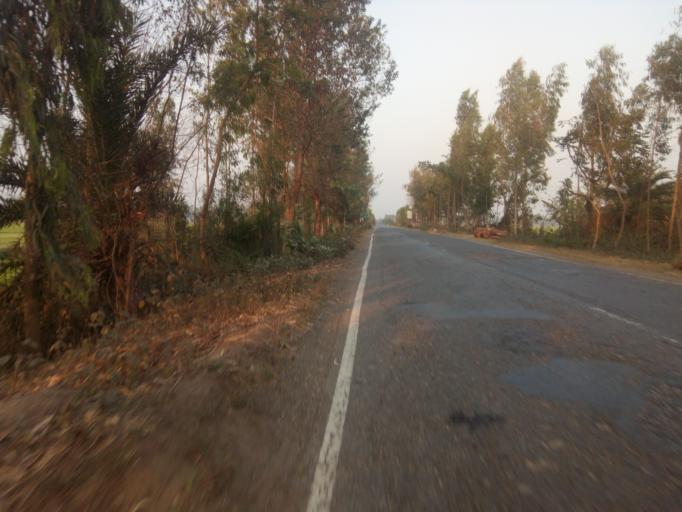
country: BD
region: Rajshahi
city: Bogra
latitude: 24.5795
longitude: 89.2235
